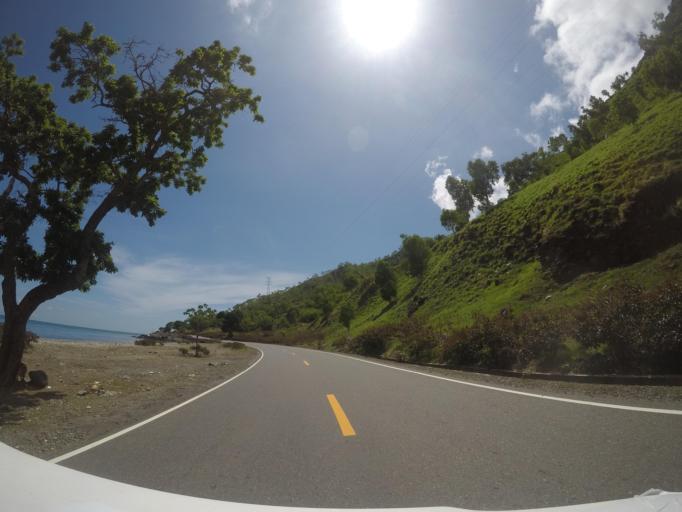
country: TL
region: Manatuto
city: Manatuto
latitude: -8.4807
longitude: 125.9245
